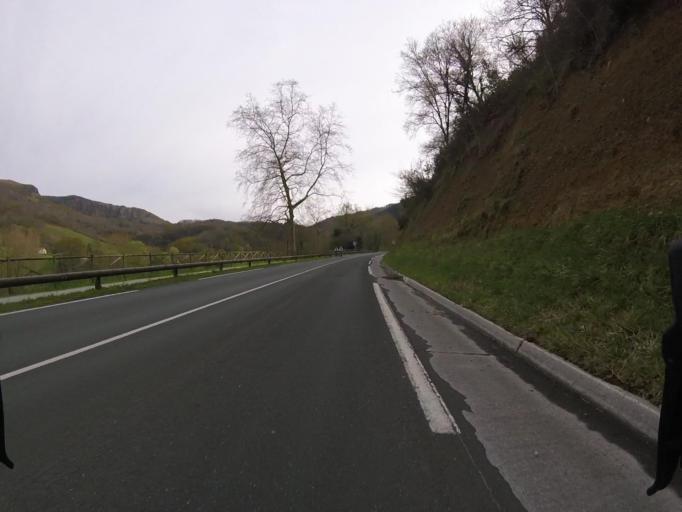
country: ES
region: Basque Country
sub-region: Provincia de Guipuzcoa
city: Irun
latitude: 43.3258
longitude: -1.7392
